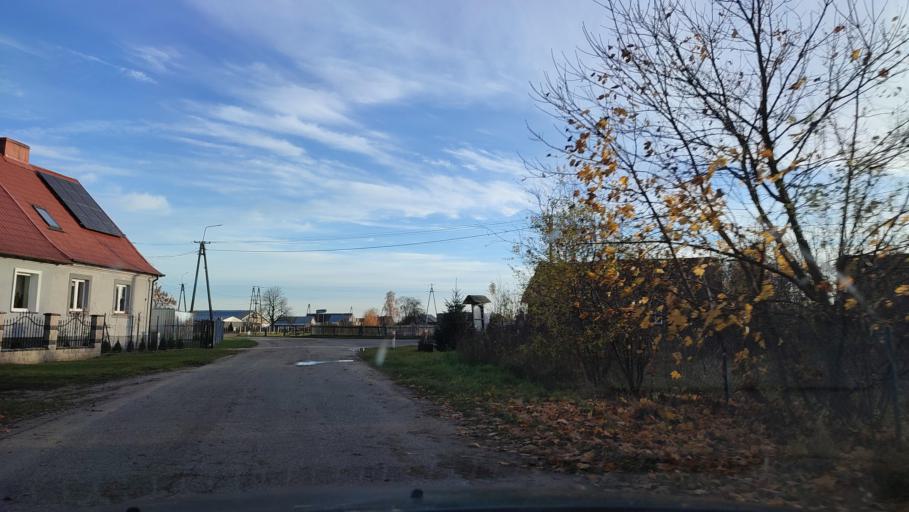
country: PL
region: Masovian Voivodeship
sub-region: Powiat przasnyski
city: Chorzele
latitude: 53.3408
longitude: 20.7541
